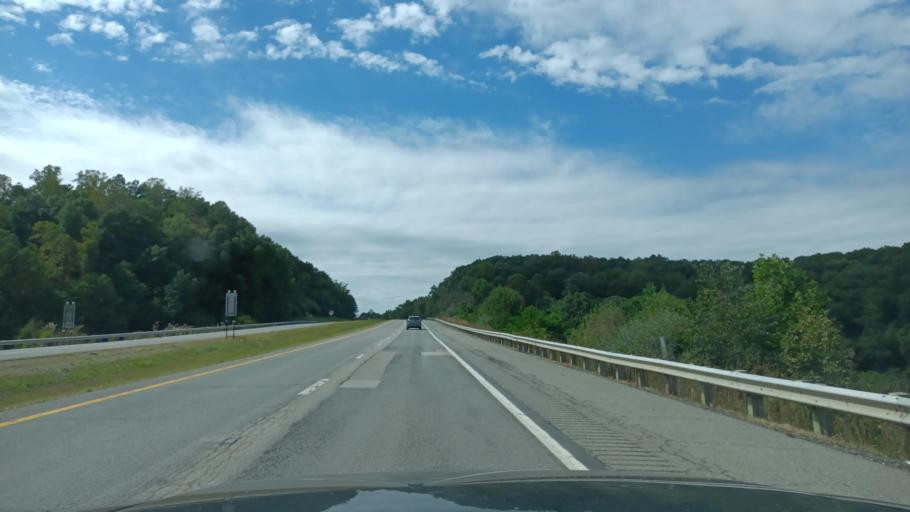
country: US
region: West Virginia
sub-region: Ritchie County
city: Harrisville
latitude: 39.2612
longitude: -81.1524
